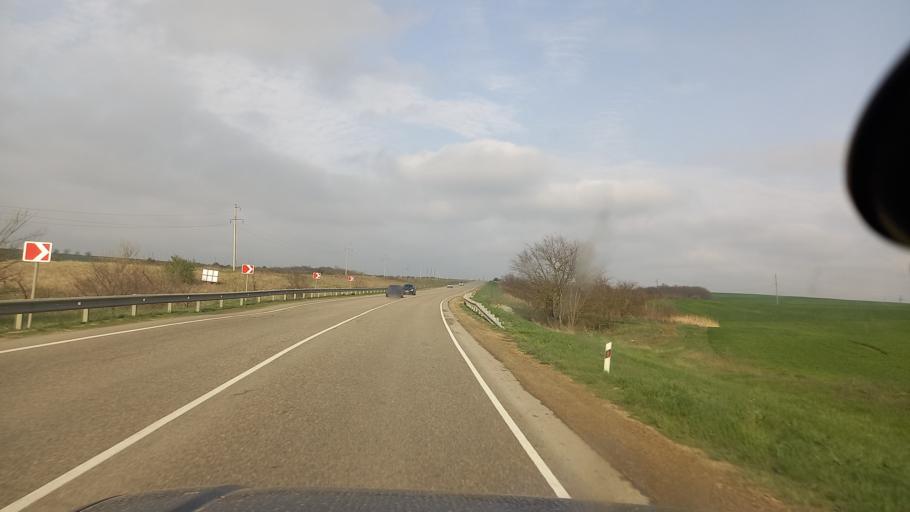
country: RU
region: Krasnodarskiy
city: Varenikovskaya
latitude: 45.0970
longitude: 37.5868
